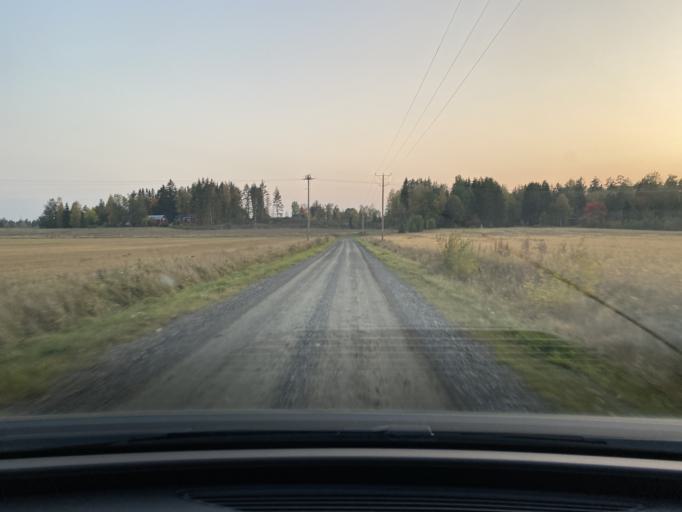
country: FI
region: Pirkanmaa
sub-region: Lounais-Pirkanmaa
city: Punkalaidun
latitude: 61.1025
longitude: 23.2115
